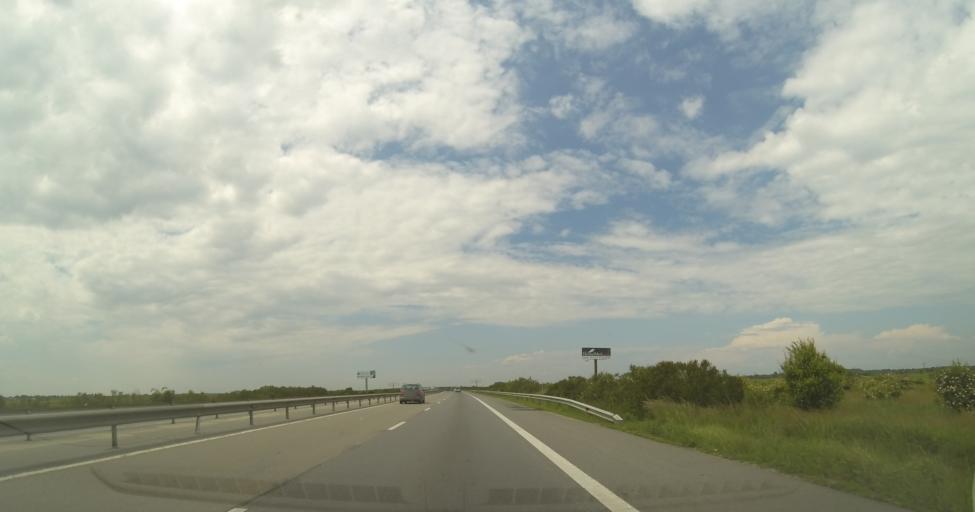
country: RO
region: Dambovita
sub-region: Comuna Uliesti
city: Uliesti
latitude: 44.6167
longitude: 25.4439
